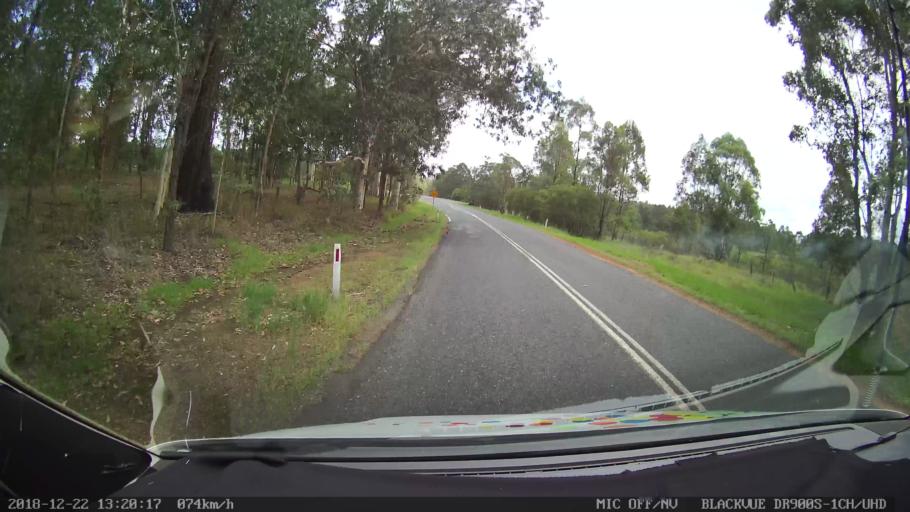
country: AU
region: New South Wales
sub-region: Clarence Valley
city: South Grafton
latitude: -29.7646
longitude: 152.9279
